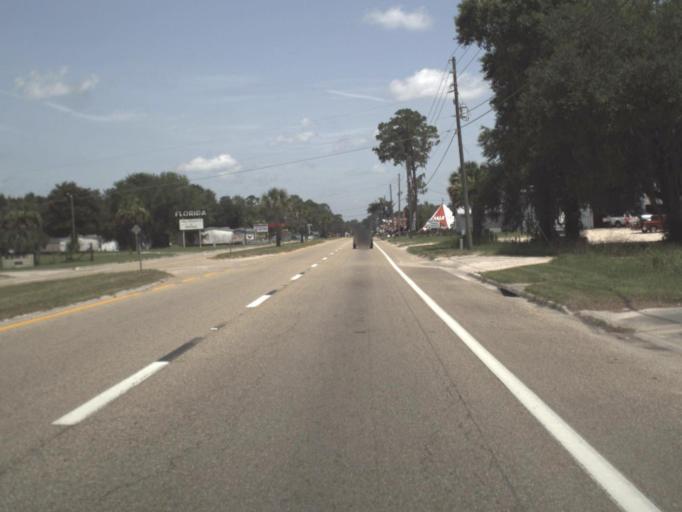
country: US
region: Florida
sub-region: Taylor County
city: Perry
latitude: 30.0721
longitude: -83.5615
